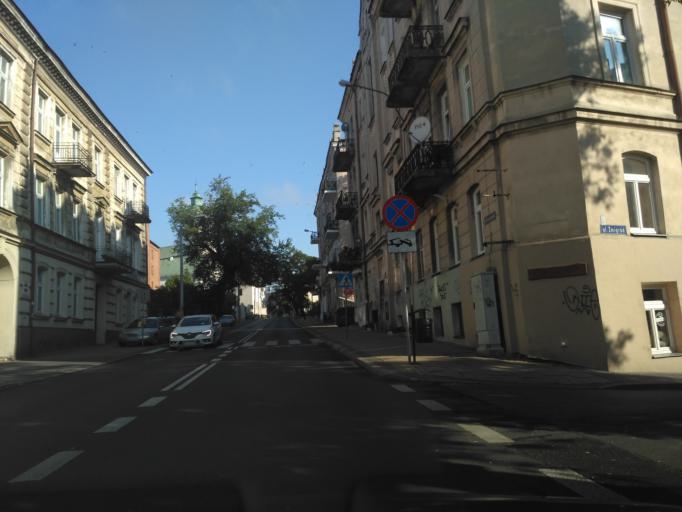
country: PL
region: Lublin Voivodeship
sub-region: Powiat lubelski
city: Lublin
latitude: 51.2449
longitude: 22.5668
